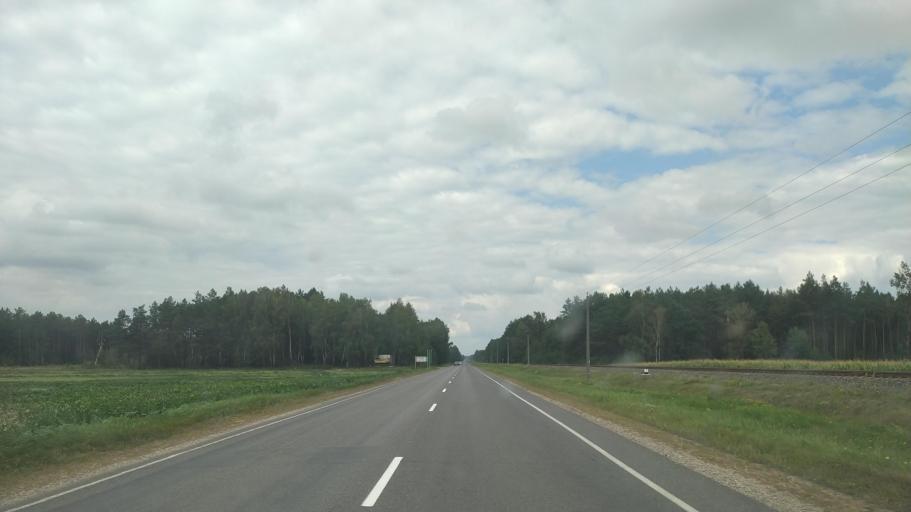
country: BY
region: Brest
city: Byelaazyorsk
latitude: 52.5207
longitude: 25.1505
